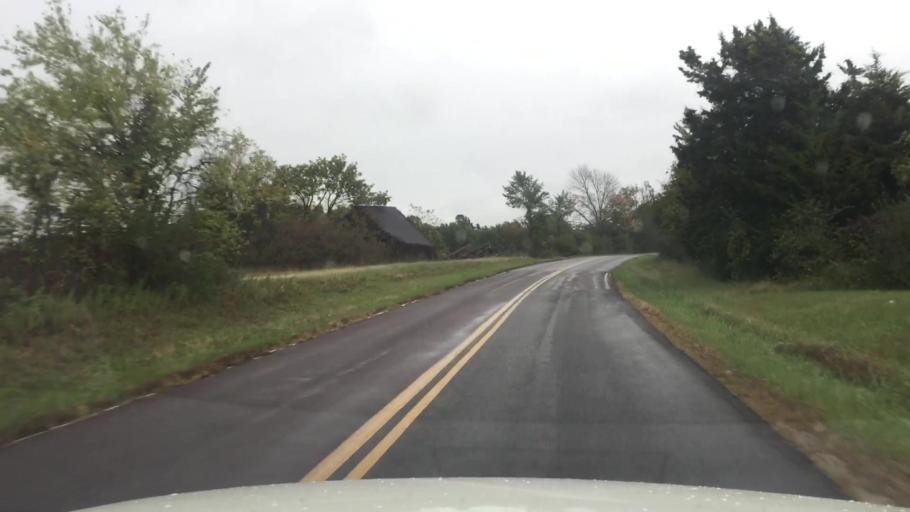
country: US
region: Missouri
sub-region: Boone County
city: Ashland
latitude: 38.7202
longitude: -92.2758
